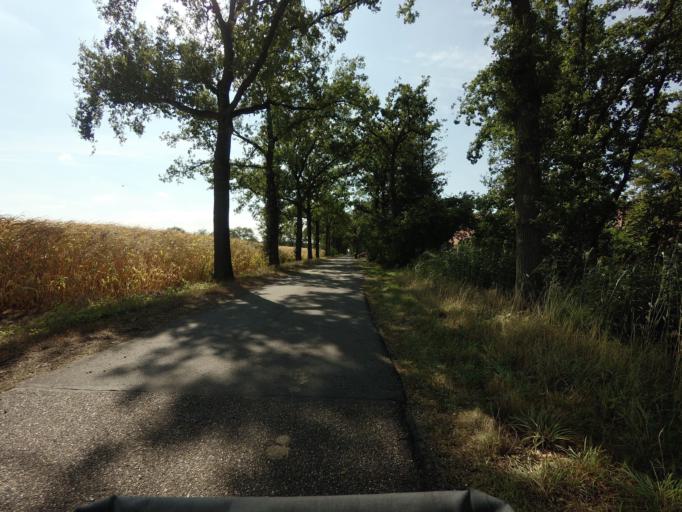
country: NL
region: North Brabant
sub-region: Gemeente Cranendonck
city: Cranendonck
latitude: 51.3268
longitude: 5.6458
